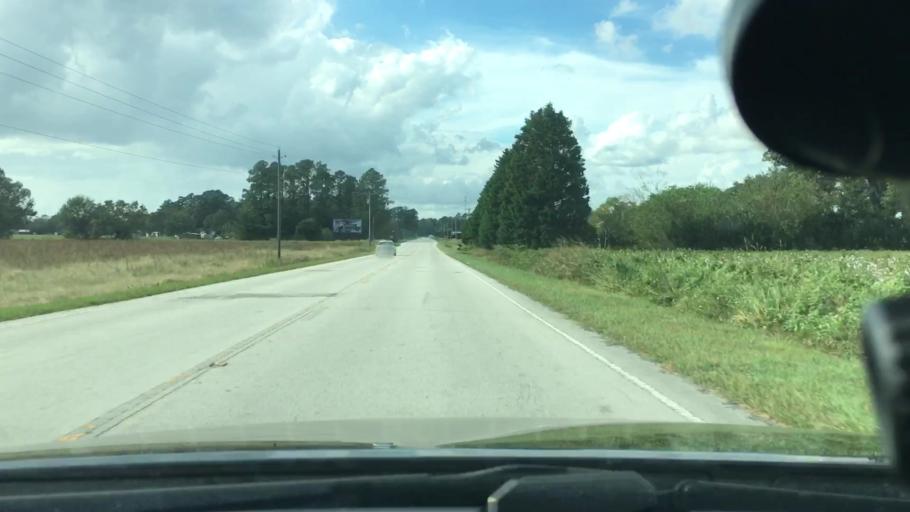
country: US
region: North Carolina
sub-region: Craven County
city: Vanceboro
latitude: 35.3755
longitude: -77.2130
